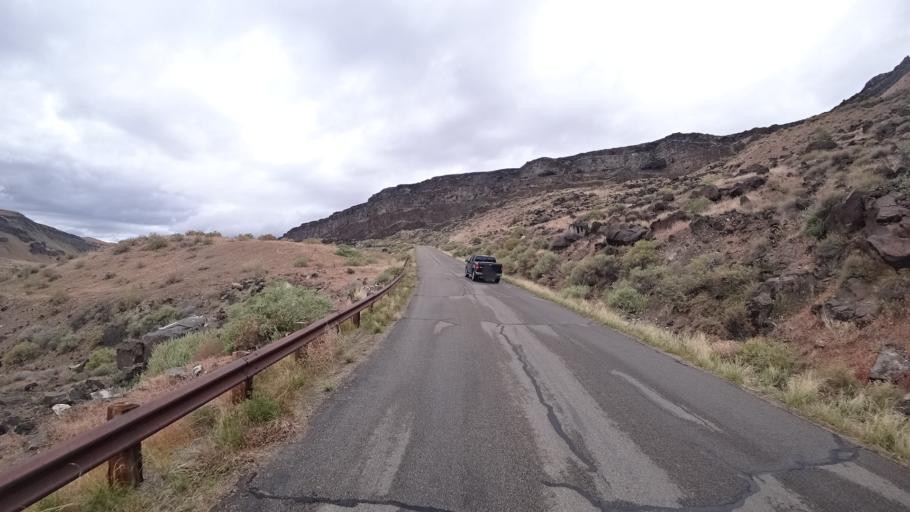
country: US
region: Idaho
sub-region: Owyhee County
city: Murphy
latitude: 43.2470
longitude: -116.3759
